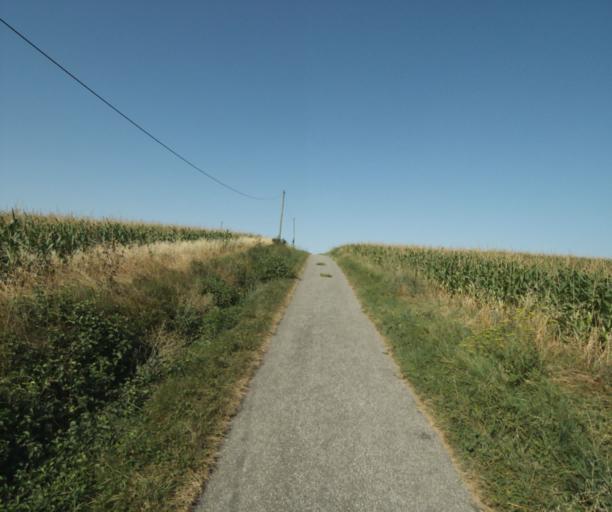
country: FR
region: Midi-Pyrenees
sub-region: Departement de la Haute-Garonne
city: Avignonet-Lauragais
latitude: 43.4259
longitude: 1.8236
